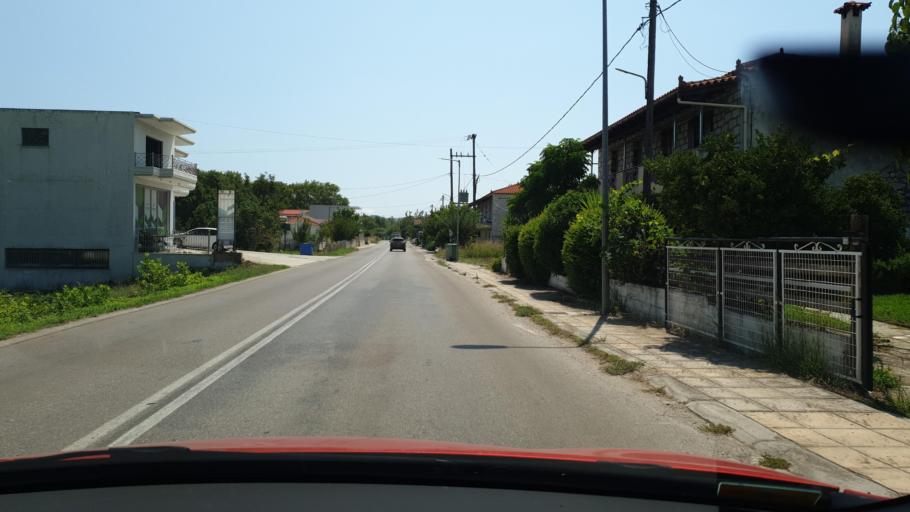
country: GR
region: Central Greece
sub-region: Nomos Evvoias
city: Aliveri
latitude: 38.4447
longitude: 24.1148
